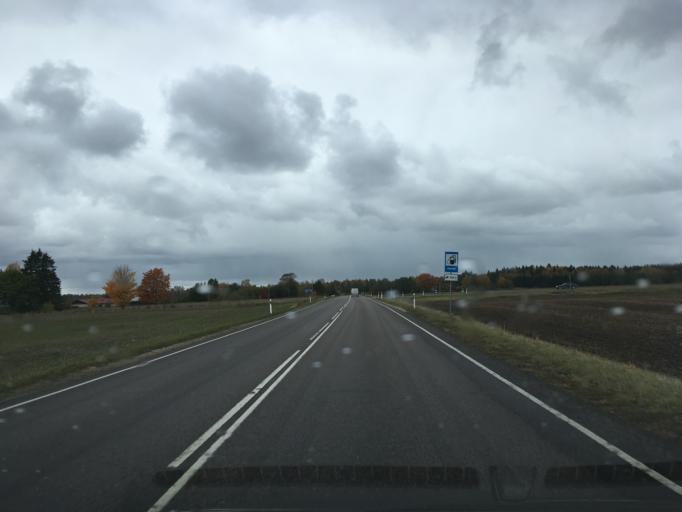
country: EE
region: Harju
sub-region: Anija vald
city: Kehra
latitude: 59.3286
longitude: 25.3227
